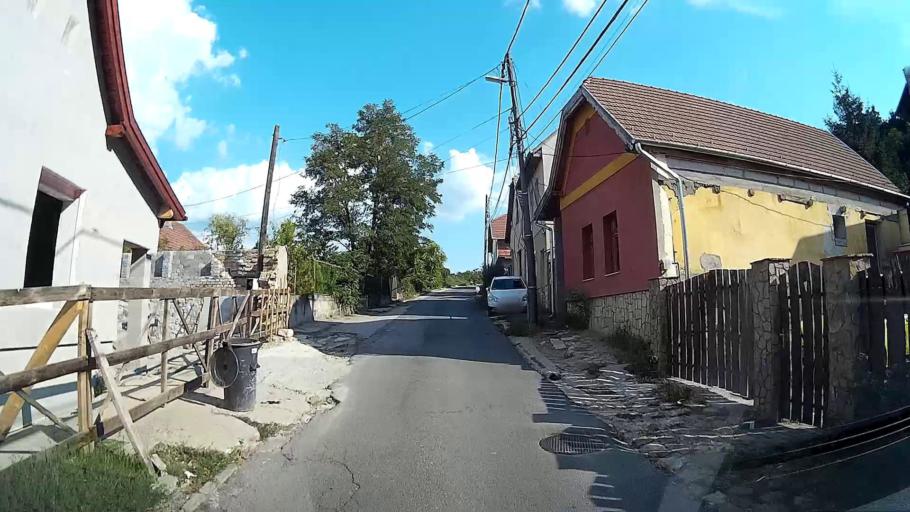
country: HU
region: Pest
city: Budakalasz
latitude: 47.6169
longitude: 19.0499
